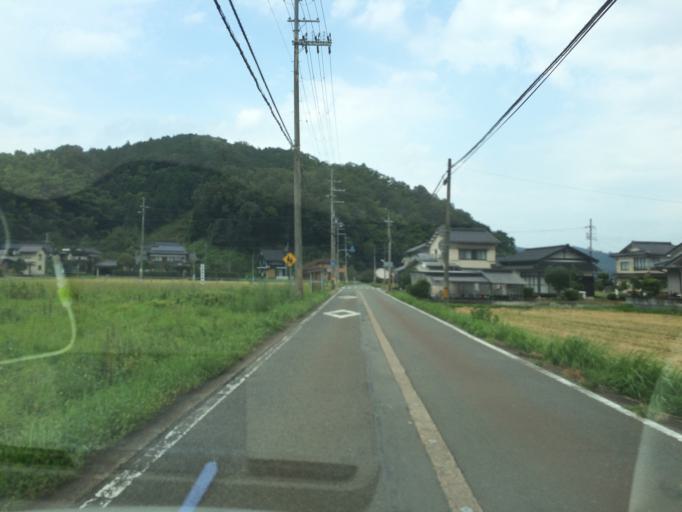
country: JP
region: Hyogo
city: Toyooka
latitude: 35.4791
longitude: 134.7766
